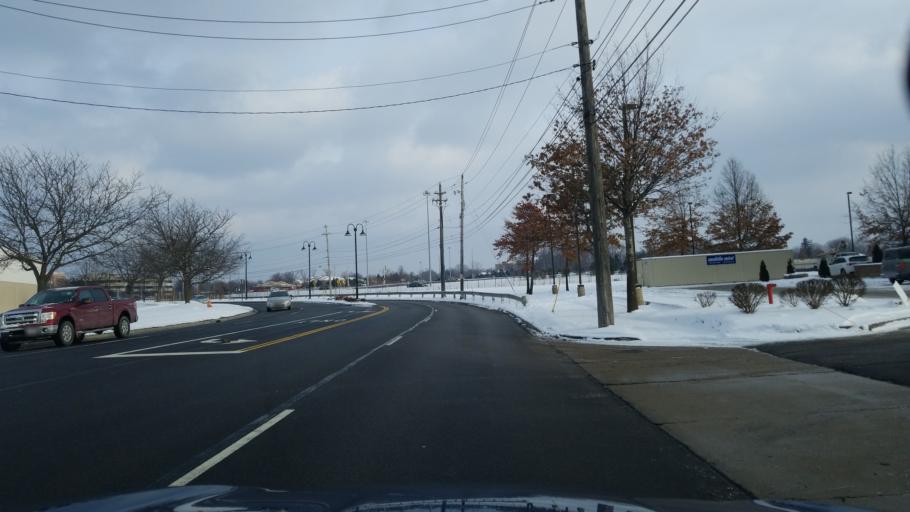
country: US
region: Ohio
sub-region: Cuyahoga County
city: North Olmsted
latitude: 41.4140
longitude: -81.9056
